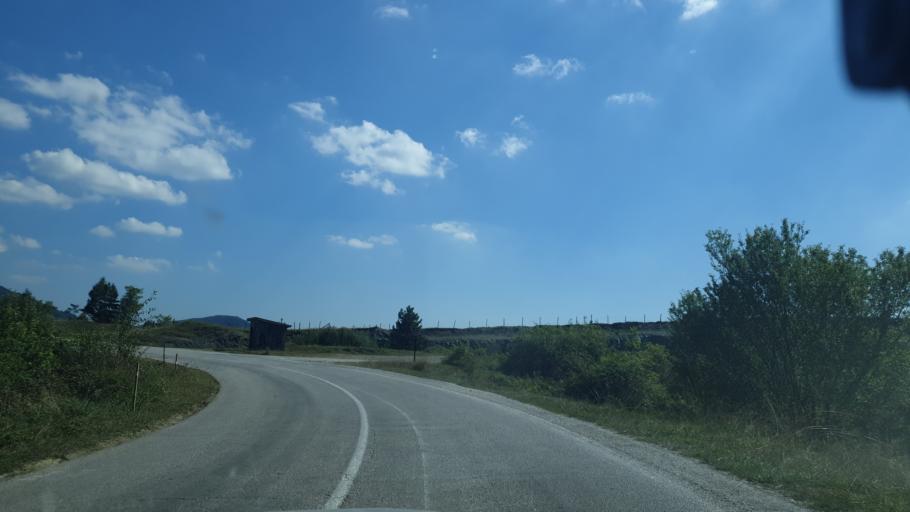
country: RS
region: Central Serbia
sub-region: Zlatiborski Okrug
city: Kosjeric
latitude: 44.0260
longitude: 20.0123
